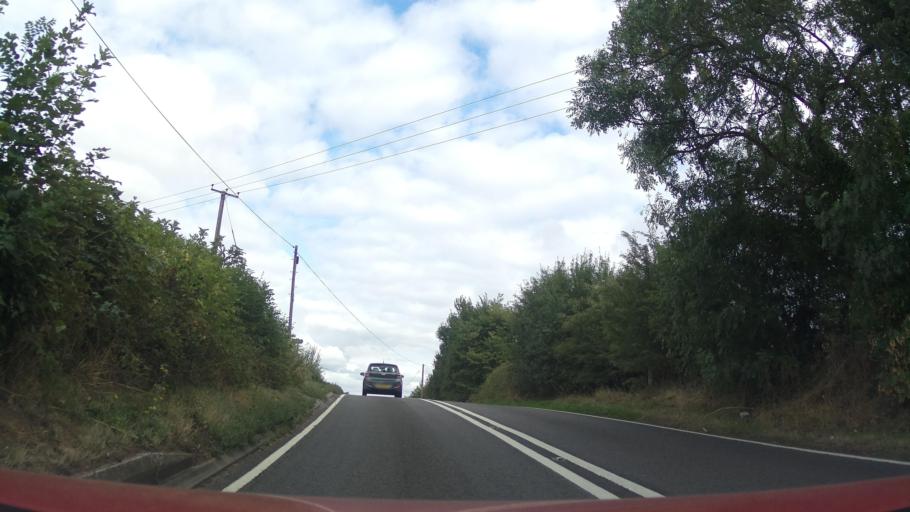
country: GB
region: England
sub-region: Leicestershire
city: Coalville
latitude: 52.7591
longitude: -1.3688
